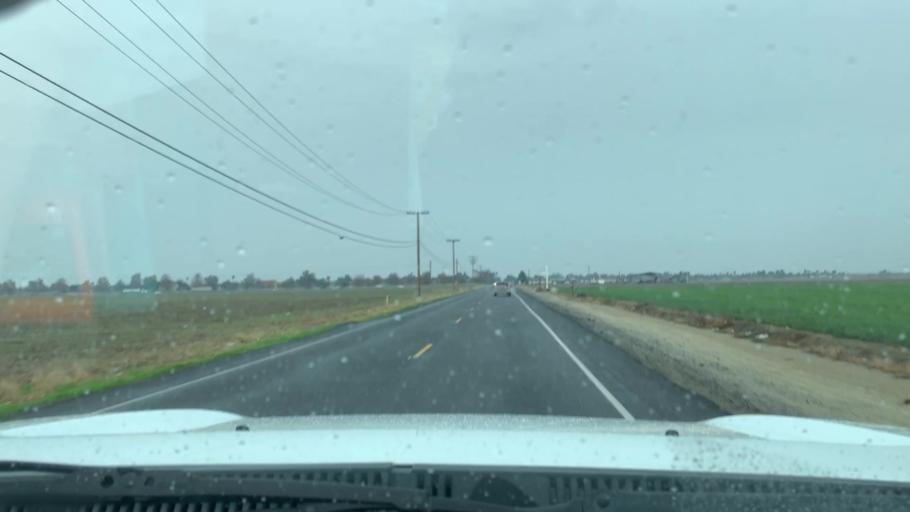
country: US
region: California
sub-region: Kern County
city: Delano
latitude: 35.7614
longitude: -119.2740
